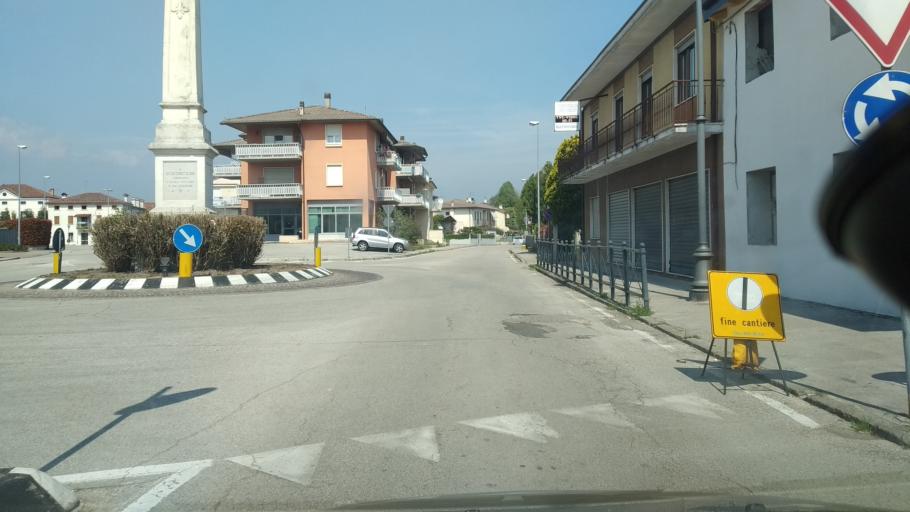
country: IT
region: Veneto
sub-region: Provincia di Vicenza
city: Dueville
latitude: 45.6288
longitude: 11.5747
